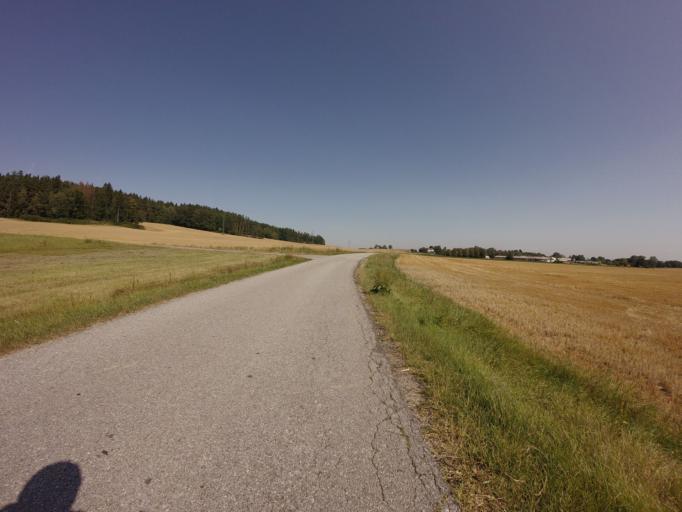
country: CZ
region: Jihocesky
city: Kamenny Ujezd
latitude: 48.8686
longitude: 14.3778
